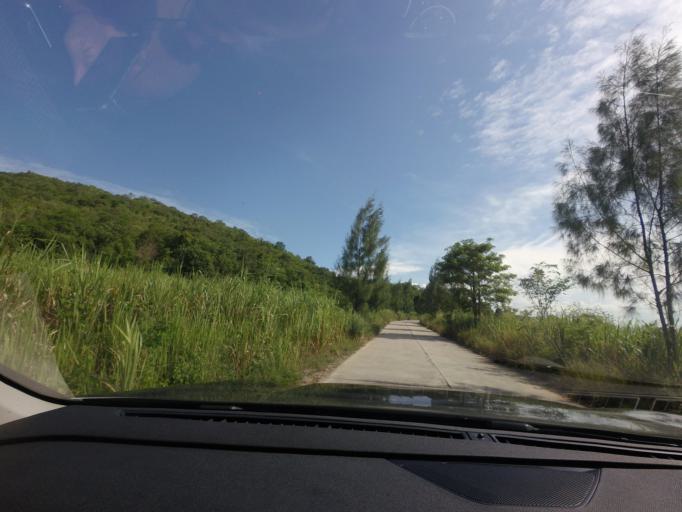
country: TH
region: Prachuap Khiri Khan
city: Hua Hin
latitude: 12.4841
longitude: 99.9431
